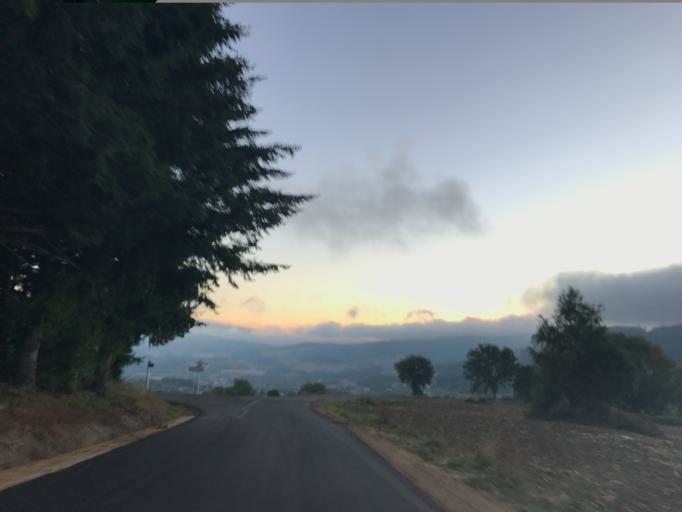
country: FR
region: Auvergne
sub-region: Departement du Puy-de-Dome
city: Celles-sur-Durolle
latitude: 45.8169
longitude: 3.6603
